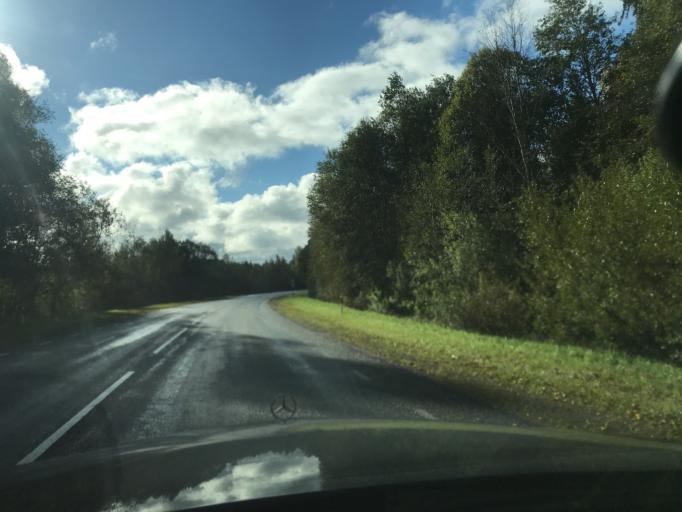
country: EE
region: Tartu
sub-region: Elva linn
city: Elva
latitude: 58.0008
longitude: 26.2681
